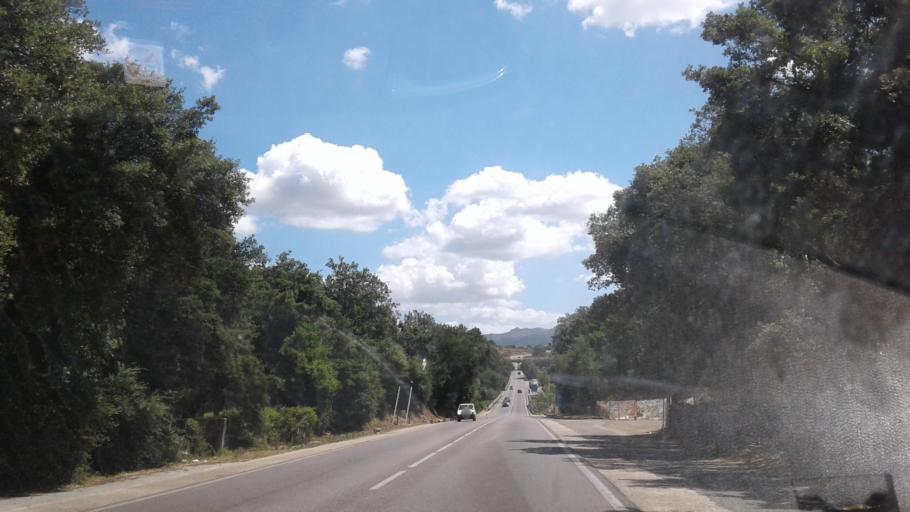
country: IT
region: Sardinia
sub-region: Provincia di Olbia-Tempio
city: Tempio Pausania
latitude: 40.9063
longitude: 9.1387
